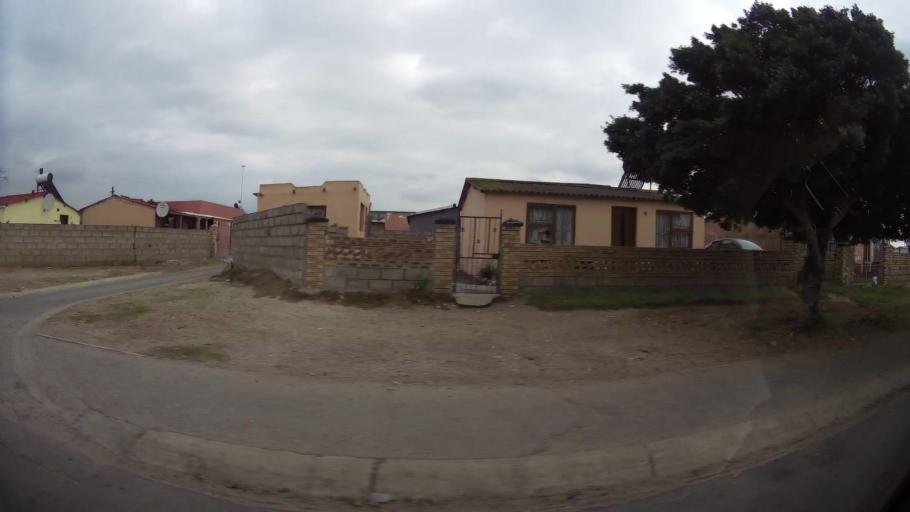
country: ZA
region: Eastern Cape
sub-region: Nelson Mandela Bay Metropolitan Municipality
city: Port Elizabeth
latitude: -33.8783
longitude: 25.5965
